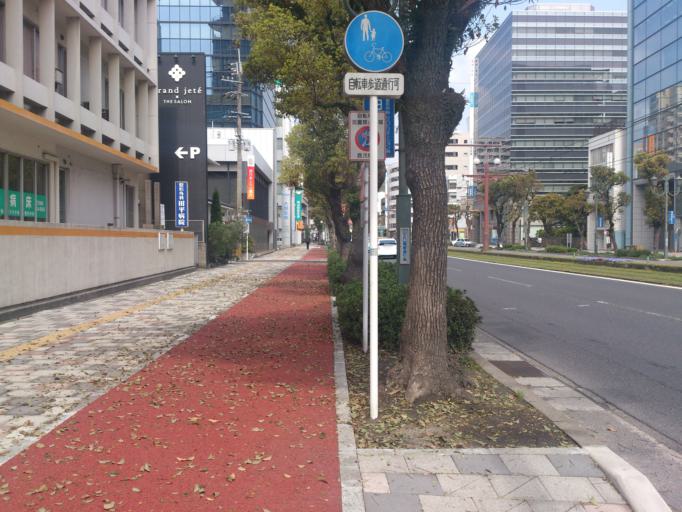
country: JP
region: Kagoshima
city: Kagoshima-shi
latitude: 31.5869
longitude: 130.5522
